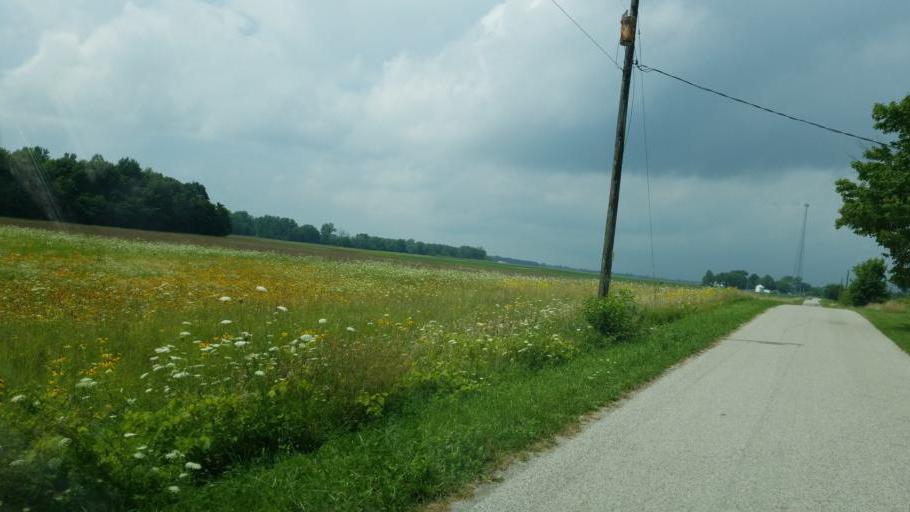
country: US
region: Ohio
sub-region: Union County
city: Richwood
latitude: 40.5081
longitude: -83.3221
